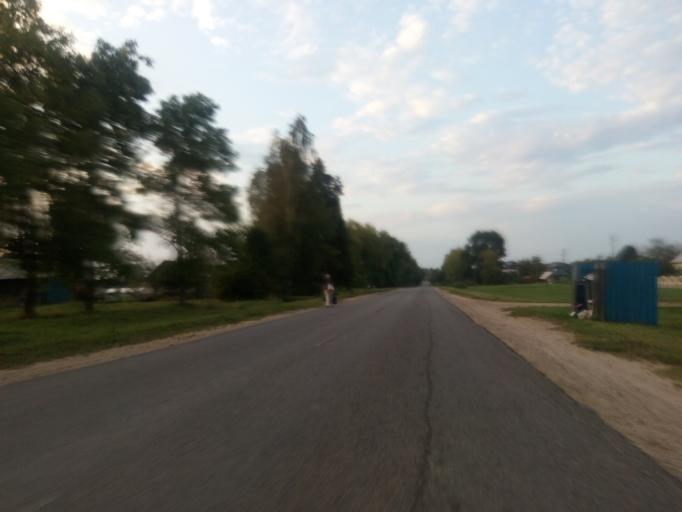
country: BY
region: Vitebsk
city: Dzisna
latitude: 55.6602
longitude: 28.3242
